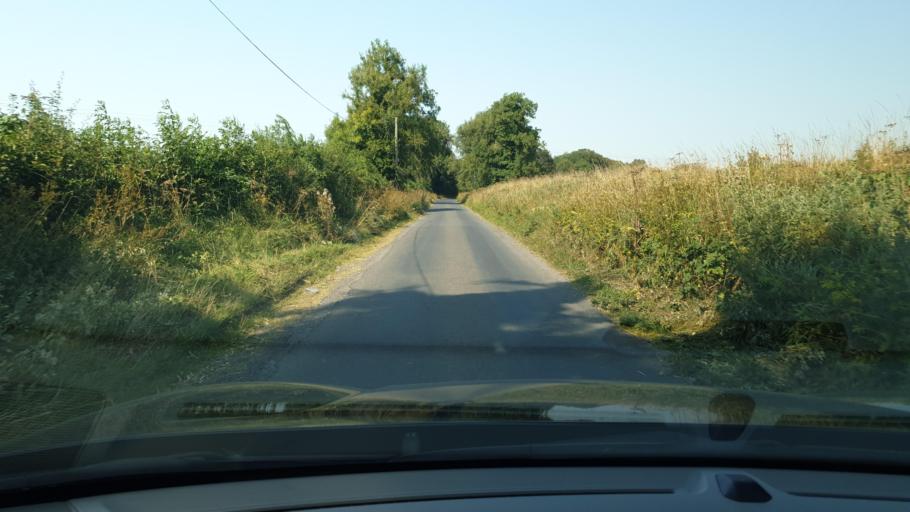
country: IE
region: Leinster
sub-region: An Mhi
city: Athboy
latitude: 53.6252
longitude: -6.9885
